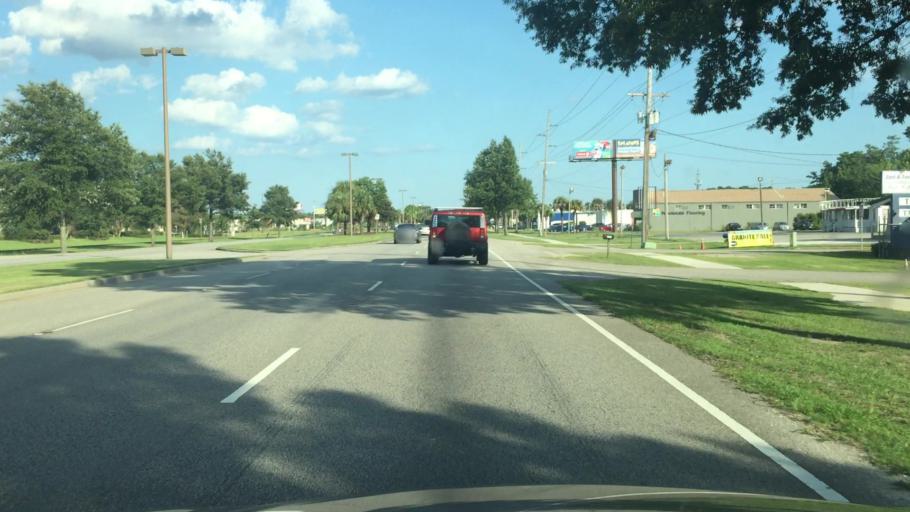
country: US
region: South Carolina
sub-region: Horry County
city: Myrtle Beach
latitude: 33.7053
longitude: -78.9090
